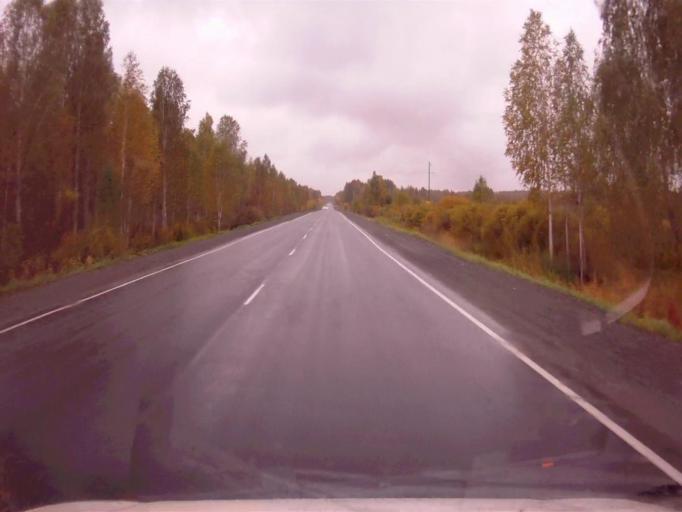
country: RU
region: Chelyabinsk
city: Argayash
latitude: 55.4789
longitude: 60.7944
